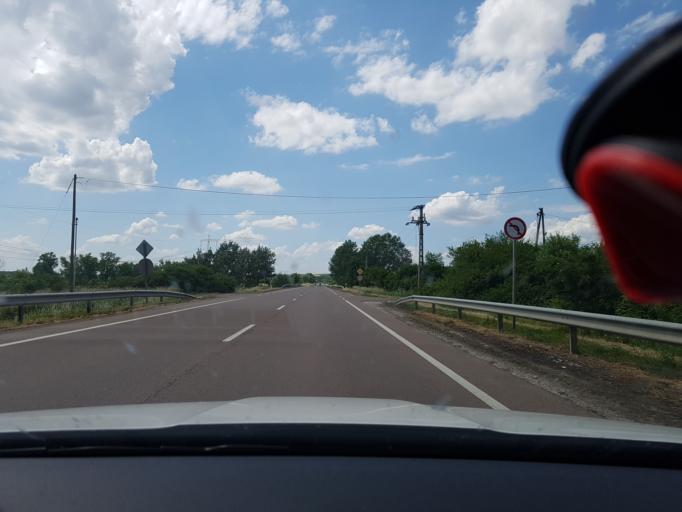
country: HU
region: Heves
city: Karacsond
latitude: 47.7404
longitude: 20.1100
